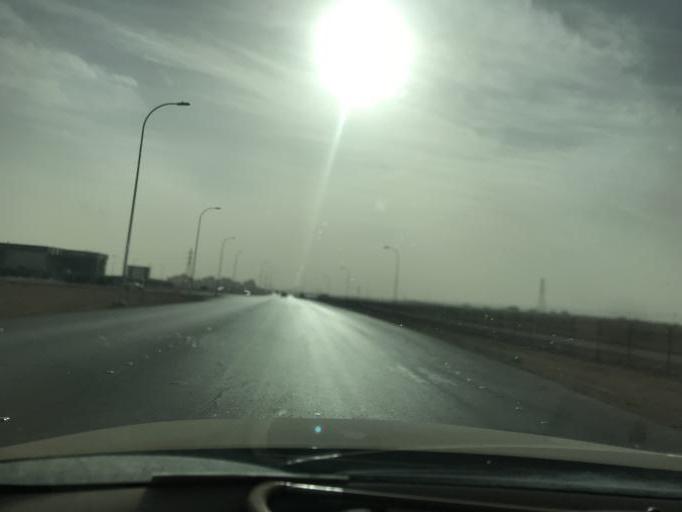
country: SA
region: Ar Riyad
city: Riyadh
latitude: 24.9206
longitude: 46.6998
